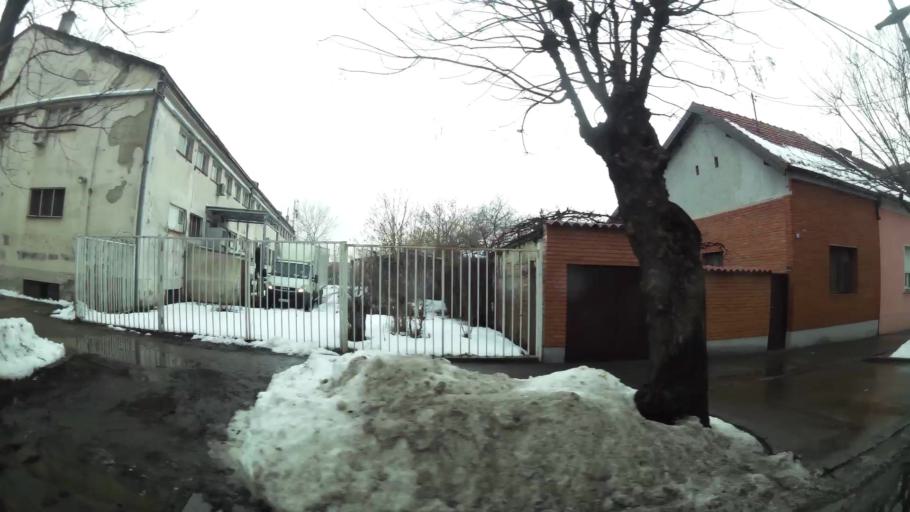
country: RS
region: Central Serbia
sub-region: Belgrade
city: Zemun
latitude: 44.8368
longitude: 20.3917
